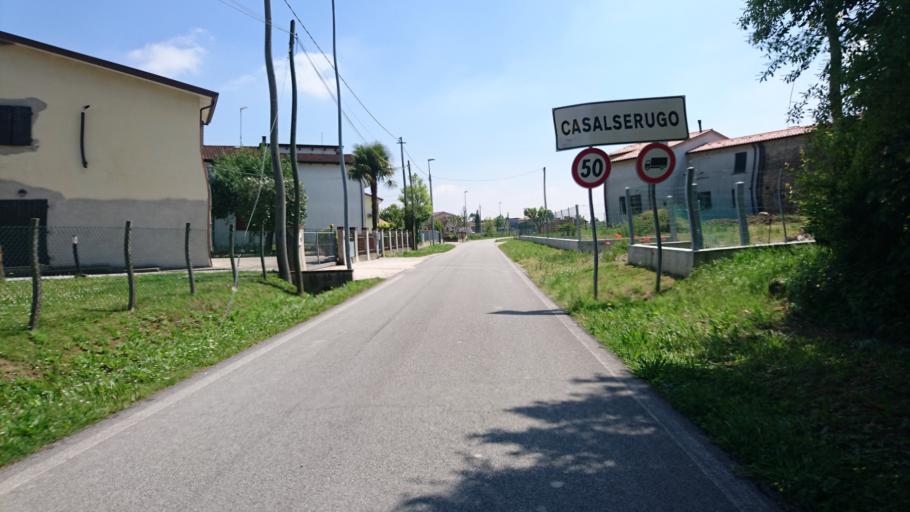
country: IT
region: Veneto
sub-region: Provincia di Padova
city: Bertipaglia
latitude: 45.3226
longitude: 11.8960
